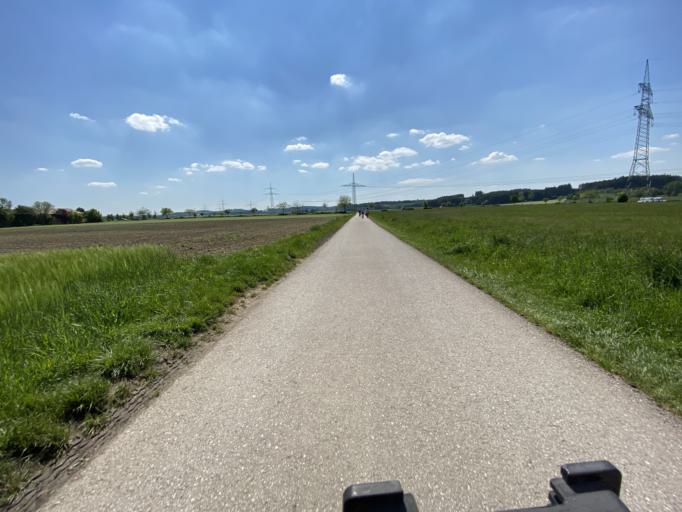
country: DE
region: Bavaria
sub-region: Upper Bavaria
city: Puchheim
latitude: 48.1324
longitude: 11.3476
